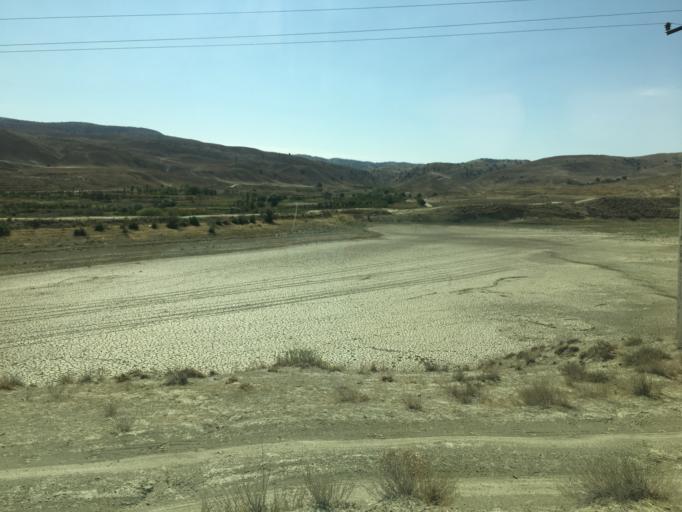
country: TM
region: Ahal
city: Baharly
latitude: 38.3799
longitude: 56.9972
